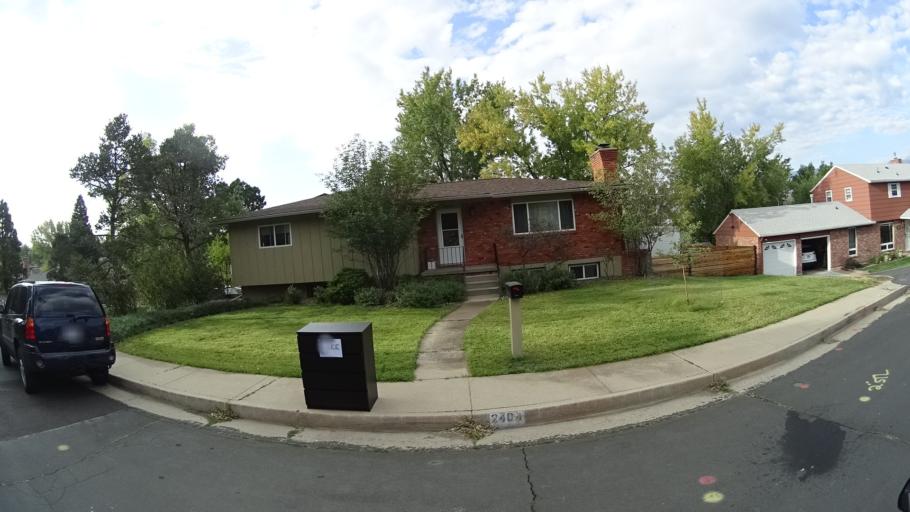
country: US
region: Colorado
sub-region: El Paso County
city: Cimarron Hills
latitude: 38.8670
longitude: -104.7523
